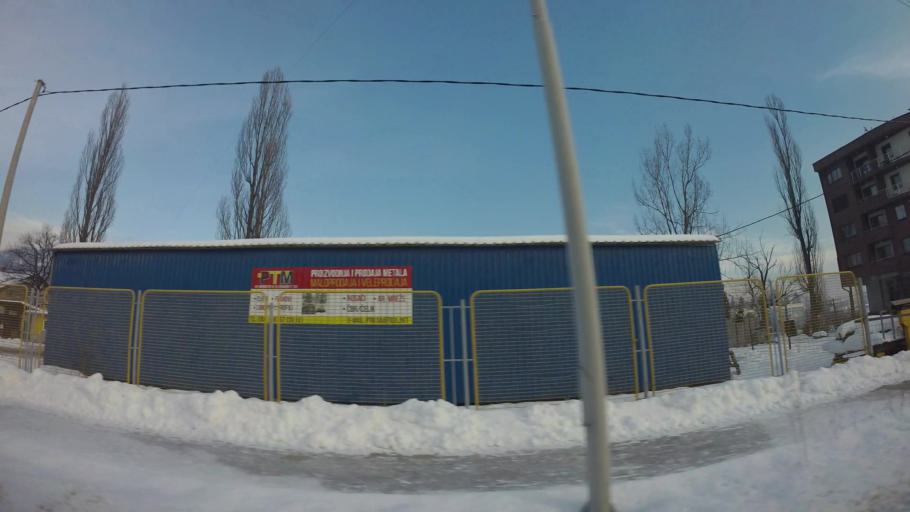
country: BA
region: Federation of Bosnia and Herzegovina
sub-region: Kanton Sarajevo
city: Sarajevo
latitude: 43.8279
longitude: 18.3647
